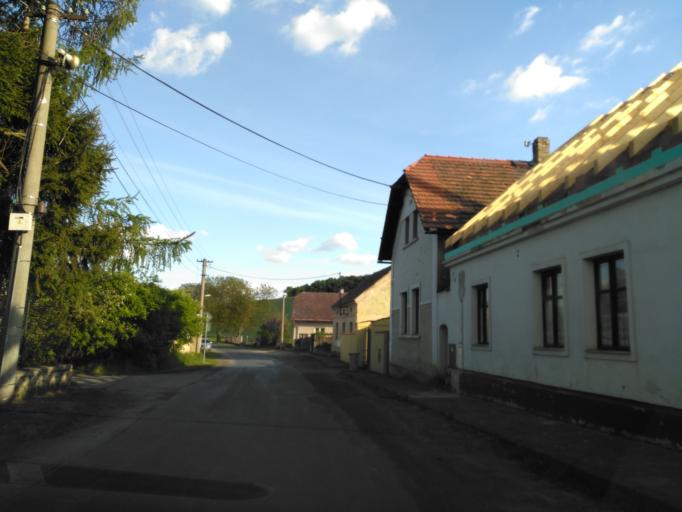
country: CZ
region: Central Bohemia
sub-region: Okres Beroun
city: Beroun
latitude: 49.8914
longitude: 14.0985
